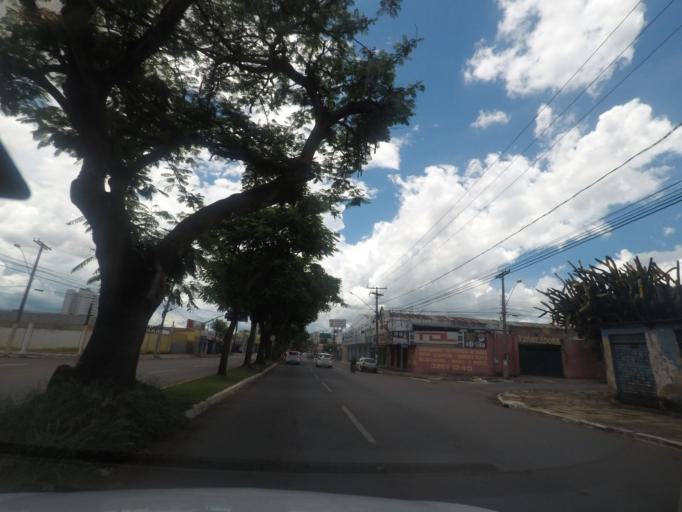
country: BR
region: Goias
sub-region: Goiania
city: Goiania
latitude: -16.6606
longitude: -49.2487
